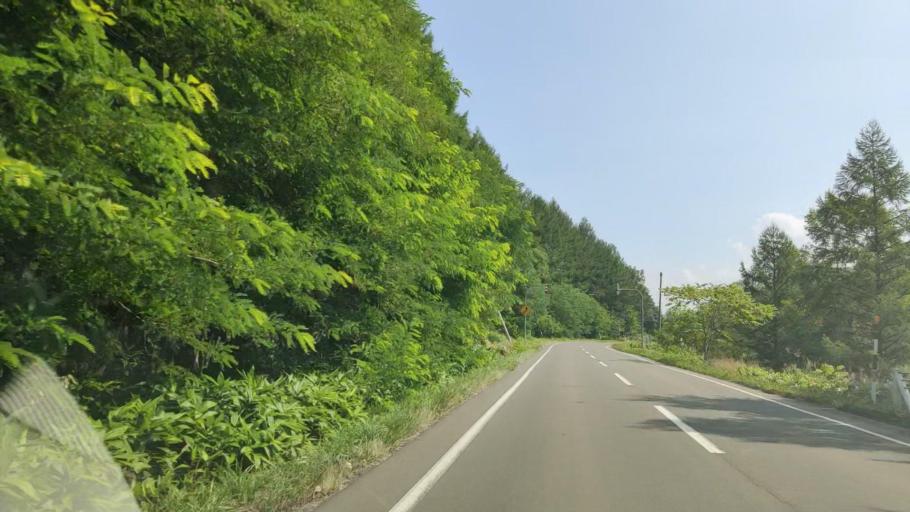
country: JP
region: Hokkaido
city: Shimo-furano
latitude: 43.4269
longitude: 142.4019
